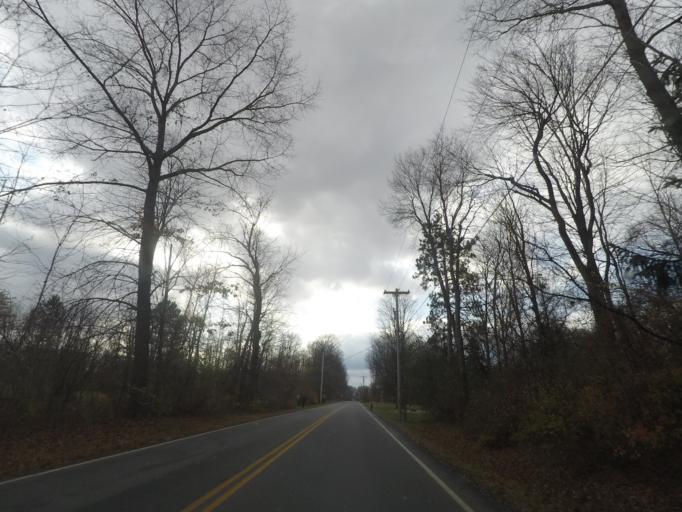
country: US
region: New York
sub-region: Saratoga County
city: Ballston Spa
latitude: 42.9957
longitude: -73.8140
